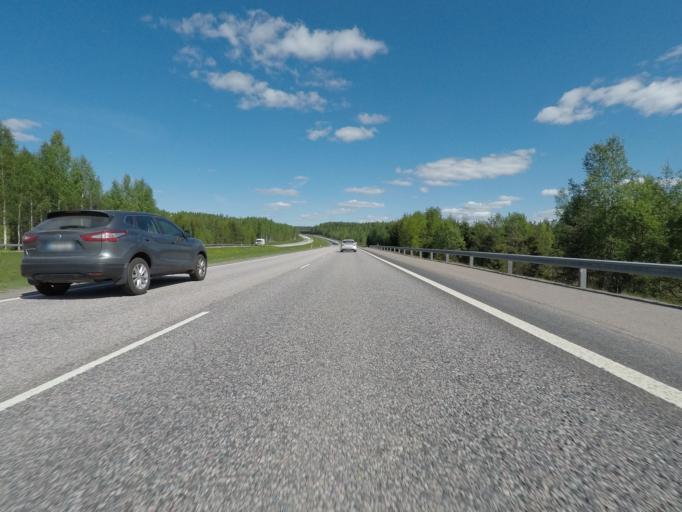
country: FI
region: Uusimaa
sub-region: Helsinki
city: Nurmijaervi
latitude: 60.4045
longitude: 24.8207
